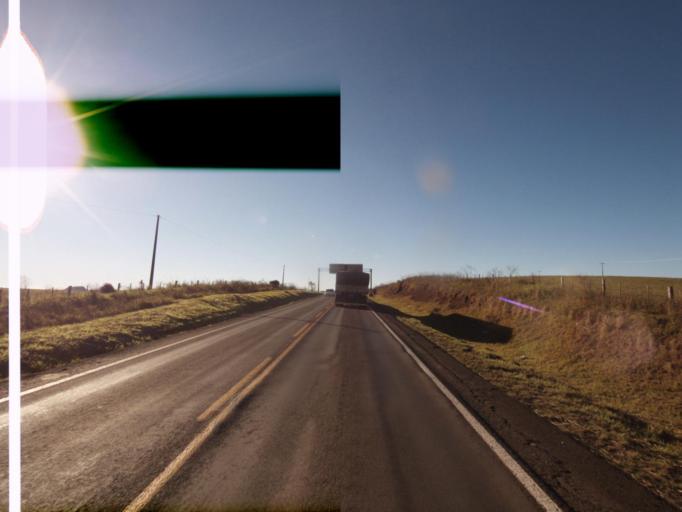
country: AR
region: Misiones
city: Bernardo de Irigoyen
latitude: -26.3000
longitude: -53.5532
